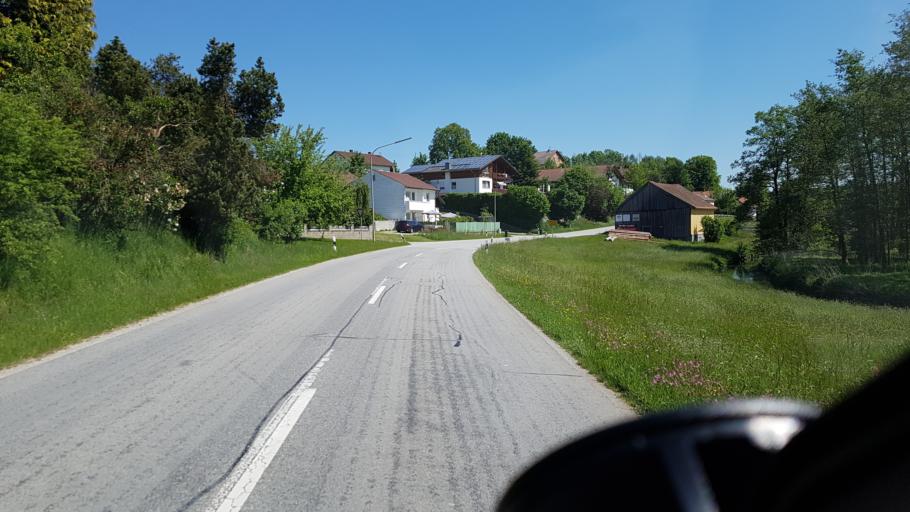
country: DE
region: Bavaria
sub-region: Lower Bavaria
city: Postmunster
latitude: 48.3664
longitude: 12.8895
